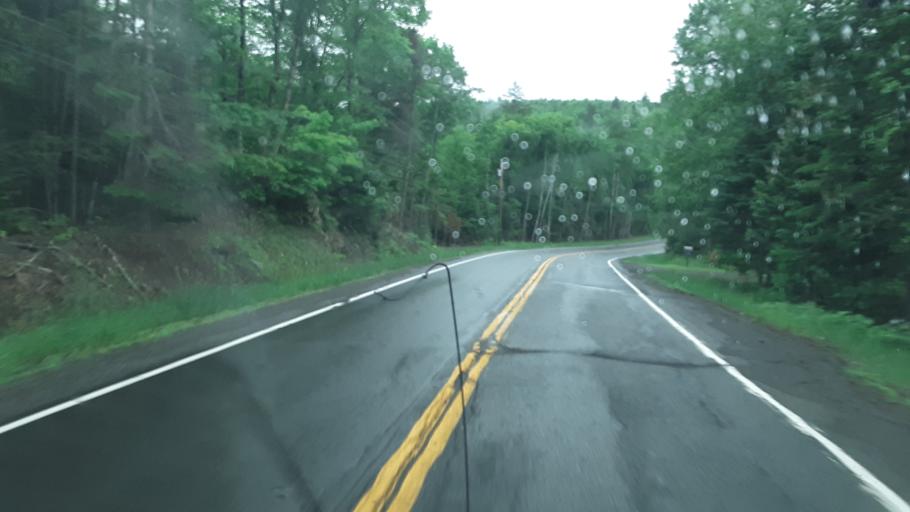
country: US
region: Maine
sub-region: Penobscot County
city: Patten
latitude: 46.1288
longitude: -68.3896
